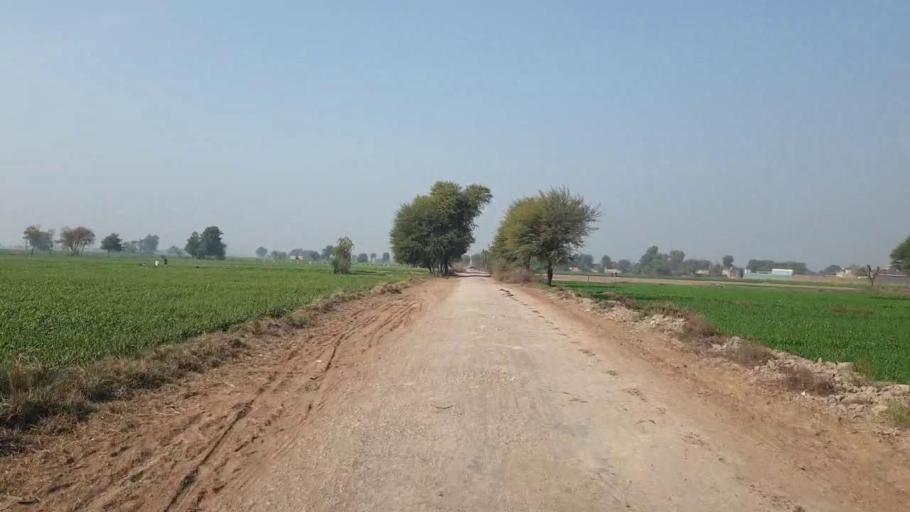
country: PK
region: Sindh
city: Bhit Shah
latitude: 25.7245
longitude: 68.5072
